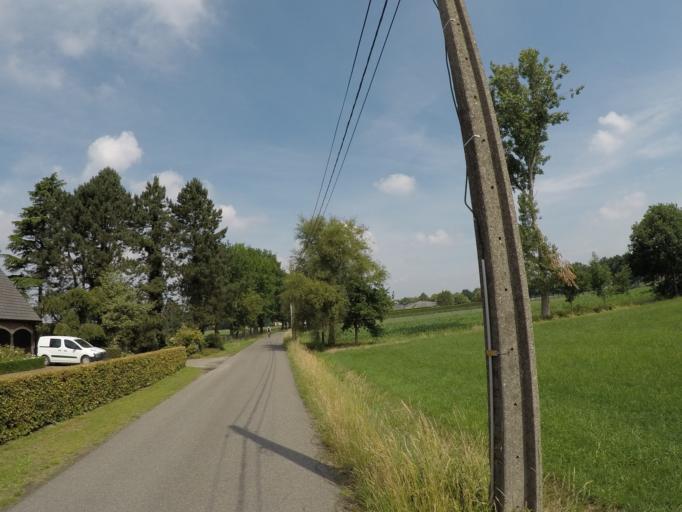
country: BE
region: Flanders
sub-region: Provincie Antwerpen
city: Brecht
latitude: 51.3442
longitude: 4.5935
